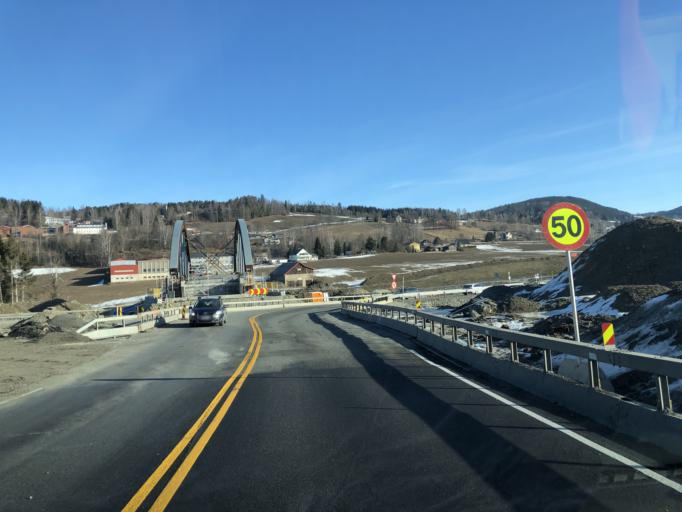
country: NO
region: Hedmark
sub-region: Ringsaker
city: Moelv
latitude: 60.9080
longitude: 10.7354
